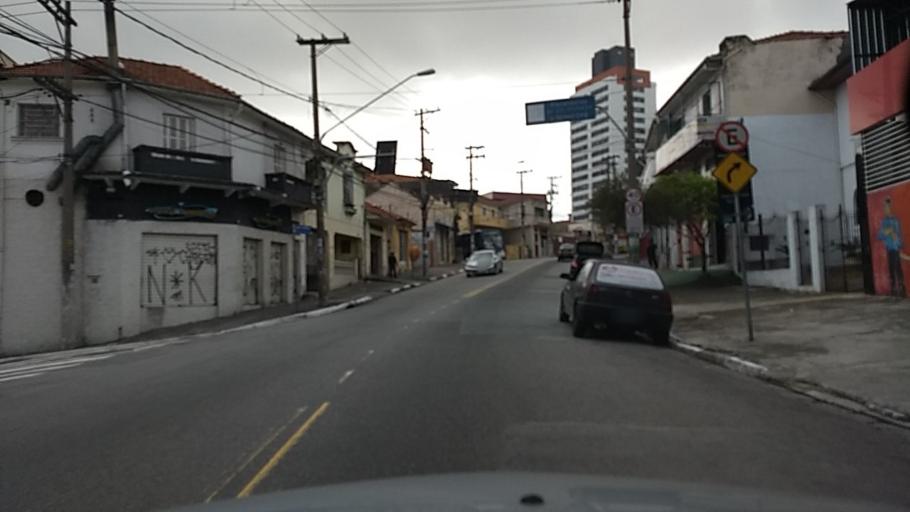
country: BR
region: Sao Paulo
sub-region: Sao Paulo
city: Sao Paulo
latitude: -23.5004
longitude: -46.6112
